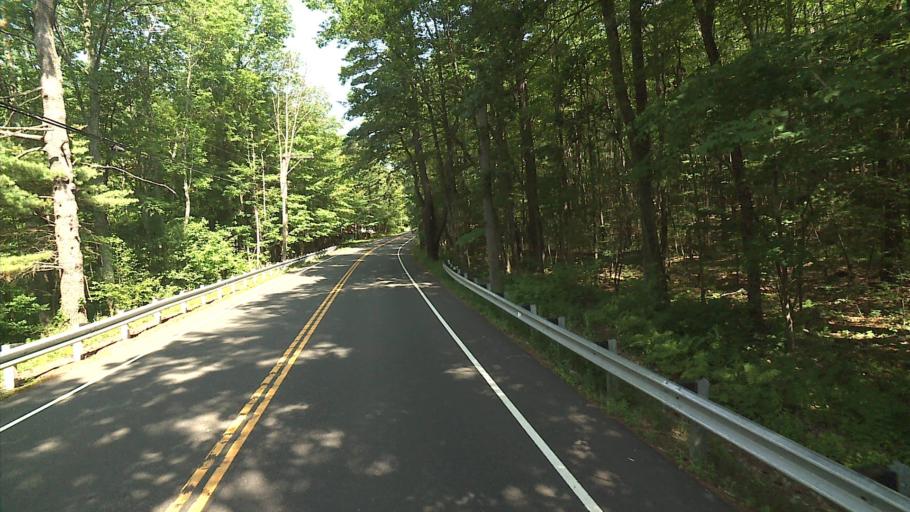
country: US
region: Massachusetts
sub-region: Berkshire County
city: New Marlborough
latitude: 42.0246
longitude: -73.2063
